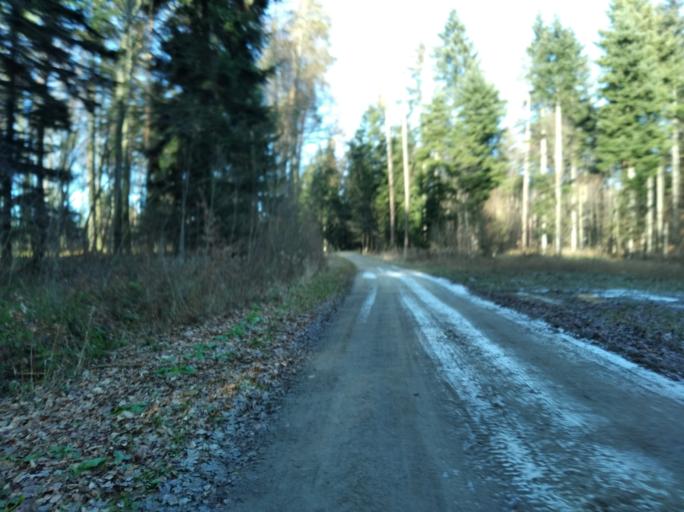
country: PL
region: Subcarpathian Voivodeship
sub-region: Powiat strzyzowski
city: Jawornik
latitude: 49.8333
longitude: 21.8585
